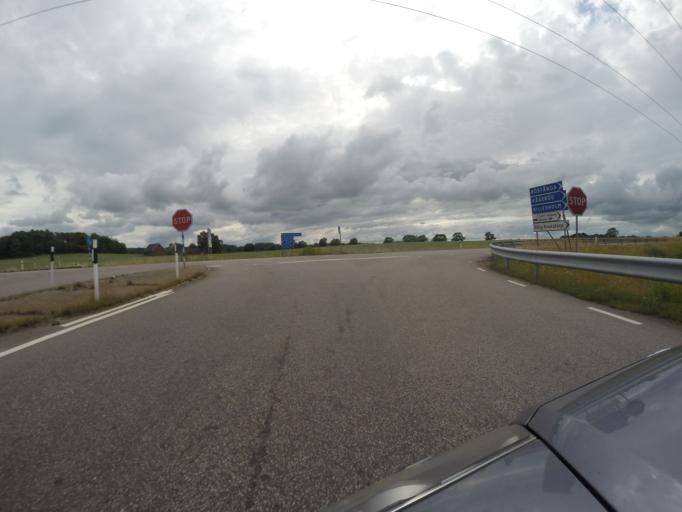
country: SE
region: Skane
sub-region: Bjuvs Kommun
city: Billesholm
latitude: 56.0559
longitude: 12.9594
